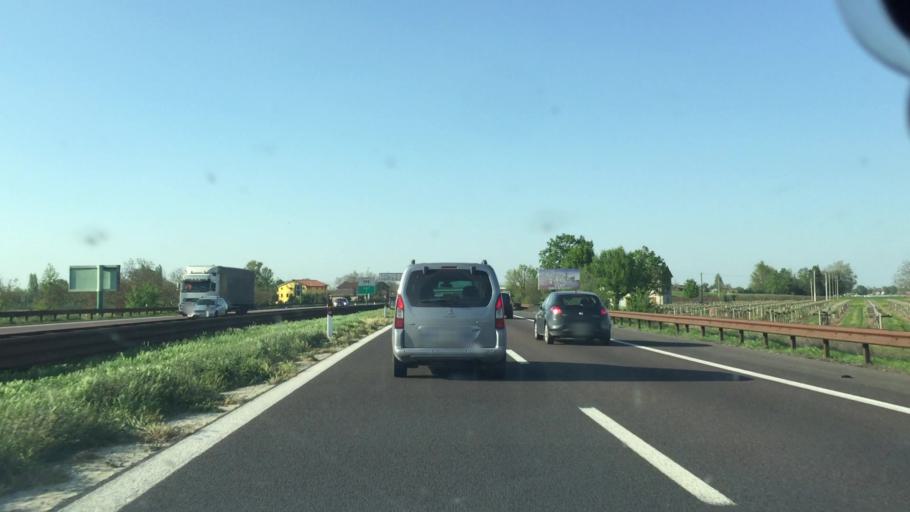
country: IT
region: Emilia-Romagna
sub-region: Provincia di Modena
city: Santa Croce Scuole
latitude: 44.7300
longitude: 10.8441
